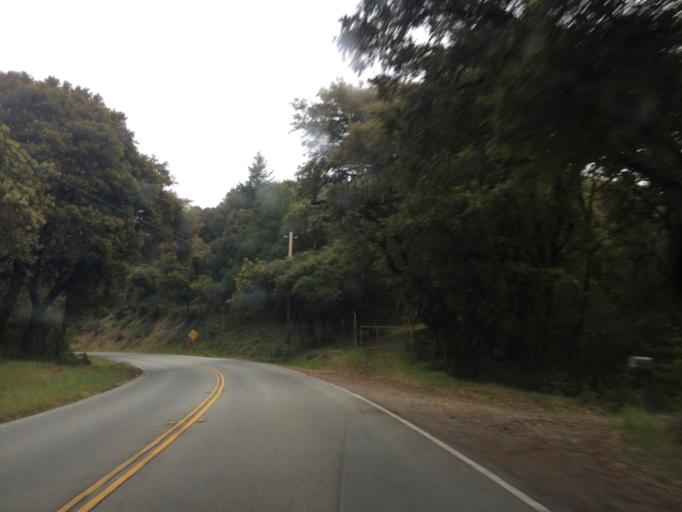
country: US
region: California
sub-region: Santa Clara County
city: Loyola
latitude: 37.2635
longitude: -122.1346
